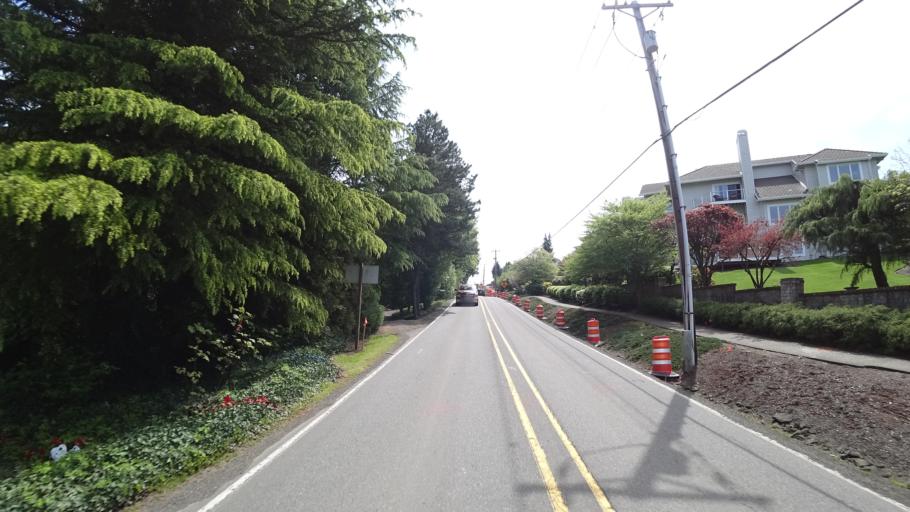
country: US
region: Oregon
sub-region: Washington County
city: Aloha
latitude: 45.4537
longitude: -122.8569
